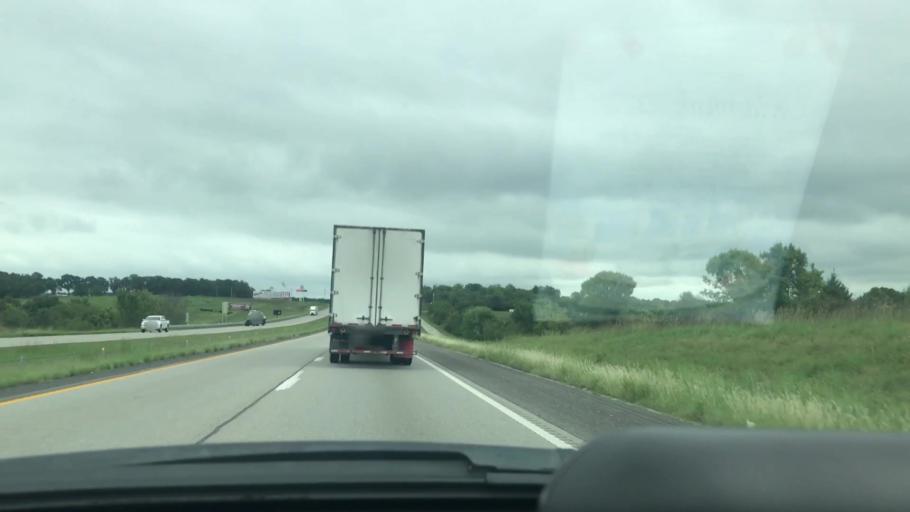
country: US
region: Missouri
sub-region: Greene County
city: Republic
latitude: 37.1859
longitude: -93.5816
